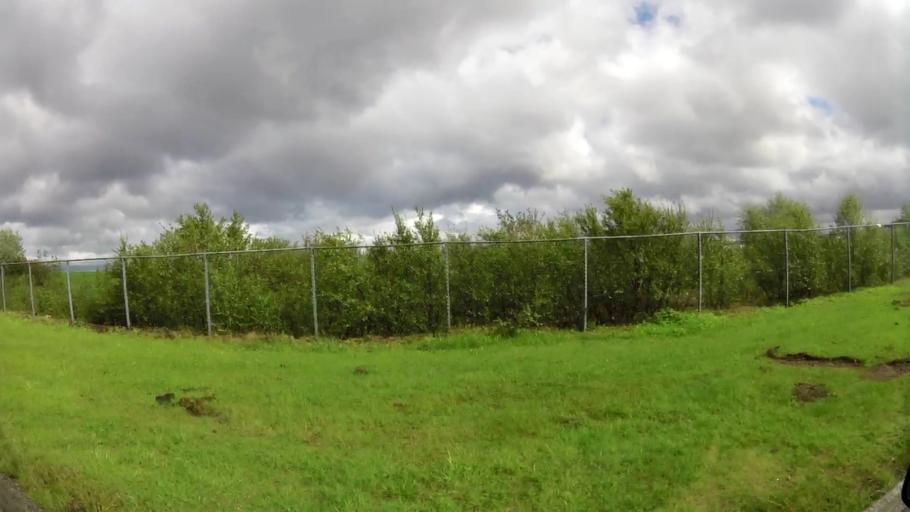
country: IS
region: Capital Region
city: Kopavogur
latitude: 64.1301
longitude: -21.9516
